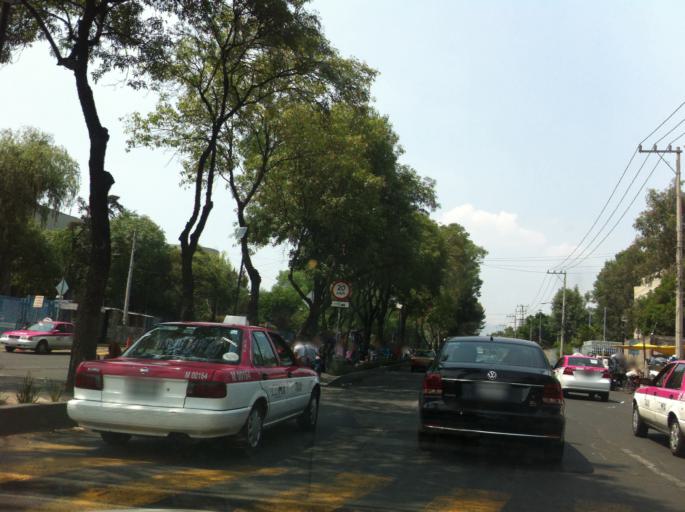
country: MX
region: Mexico
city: Colonia Lindavista
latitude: 19.4808
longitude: -99.1354
